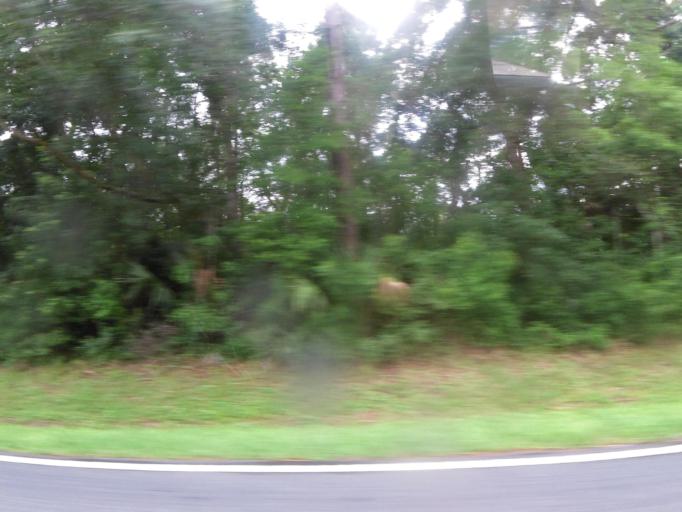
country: US
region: Florida
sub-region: Duval County
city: Jacksonville Beach
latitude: 30.2852
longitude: -81.4339
